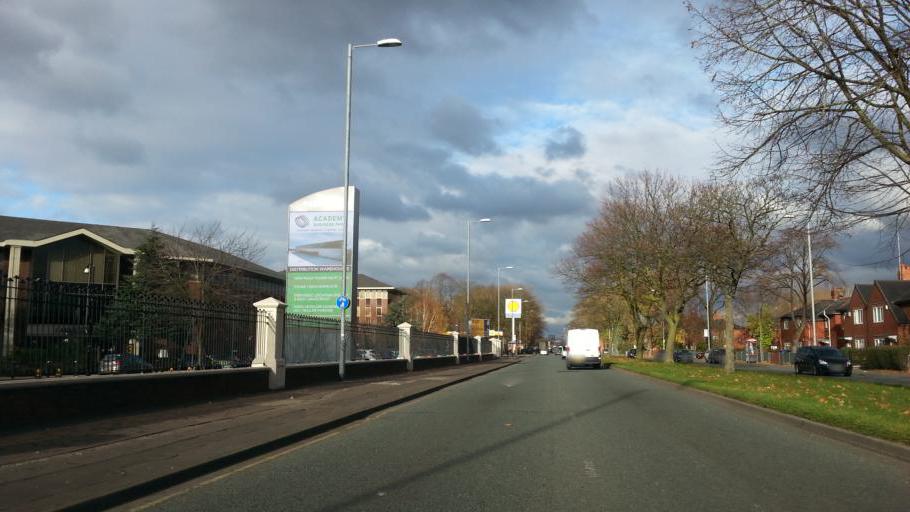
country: GB
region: England
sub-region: Manchester
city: Hulme
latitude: 53.4472
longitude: -2.2446
